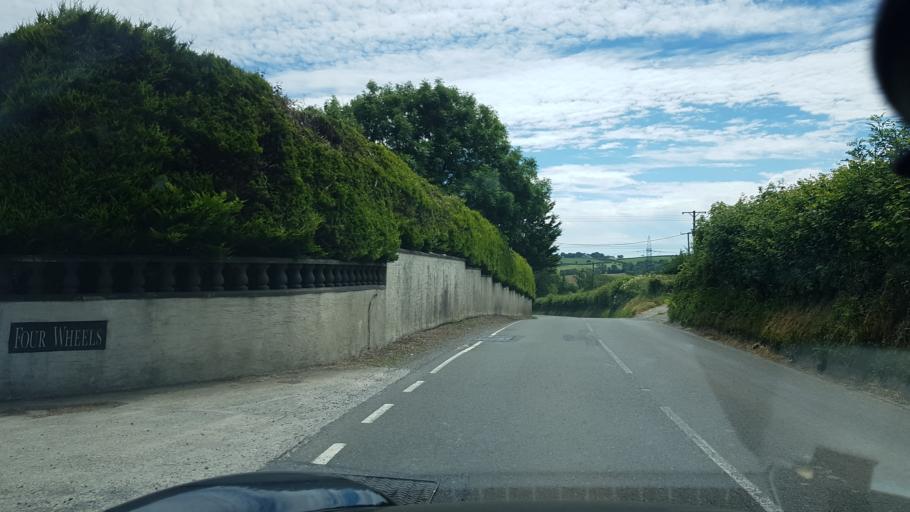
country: GB
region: Wales
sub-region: Carmarthenshire
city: Saint Clears
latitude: 51.7996
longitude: -4.4901
